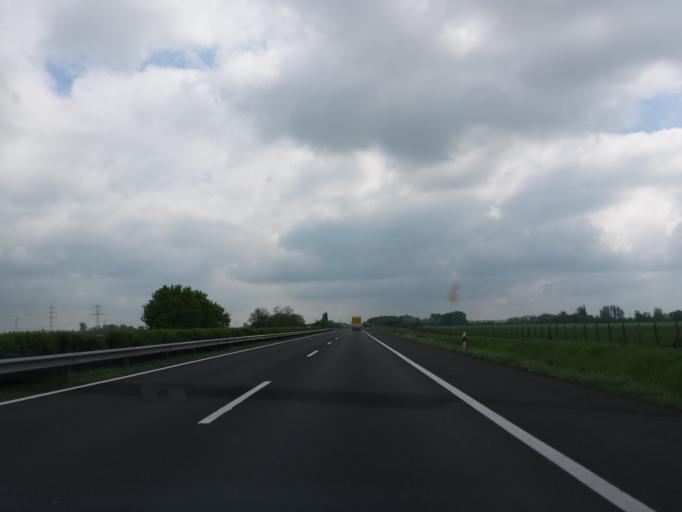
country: HU
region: Gyor-Moson-Sopron
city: Lebeny
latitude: 47.7693
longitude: 17.3768
